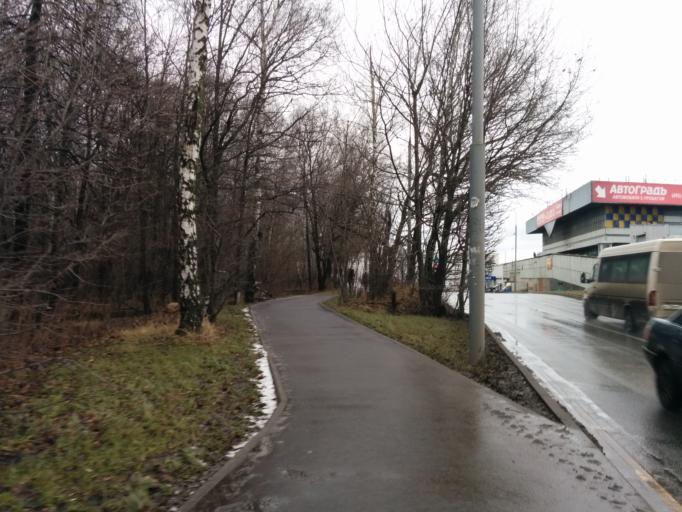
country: RU
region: Moscow
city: Chertanovo Yuzhnoye
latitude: 55.5811
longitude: 37.5858
